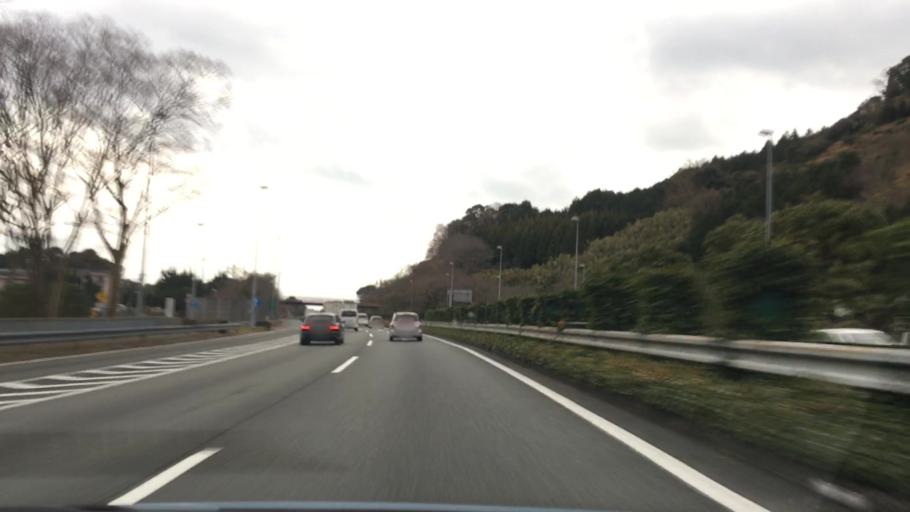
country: JP
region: Shizuoka
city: Fujinomiya
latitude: 35.1576
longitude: 138.6179
